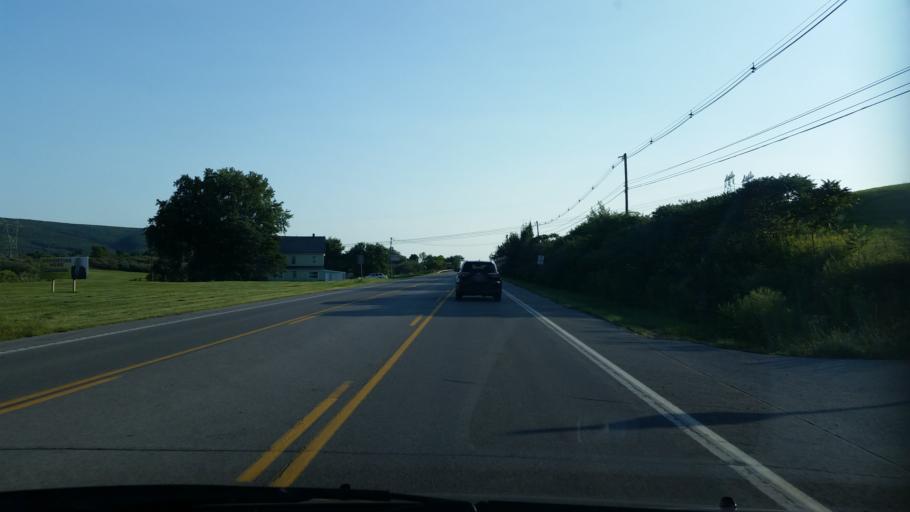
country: US
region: Pennsylvania
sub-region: Blair County
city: Bellwood
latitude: 40.5802
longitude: -78.3287
